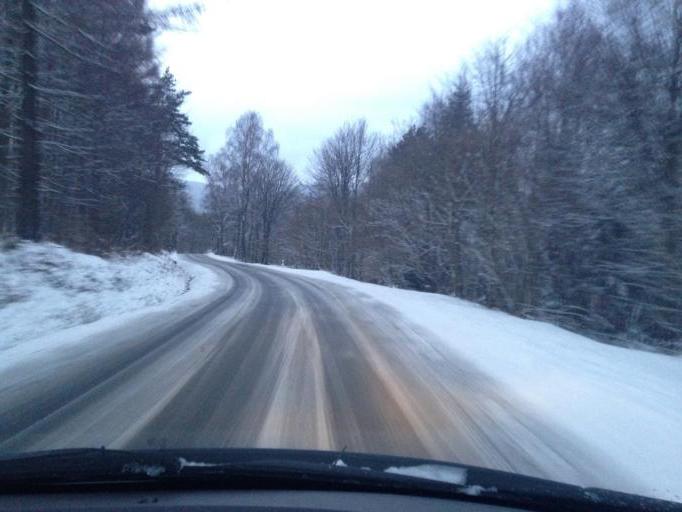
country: PL
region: Subcarpathian Voivodeship
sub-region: Powiat jasielski
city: Krempna
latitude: 49.5268
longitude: 21.5013
